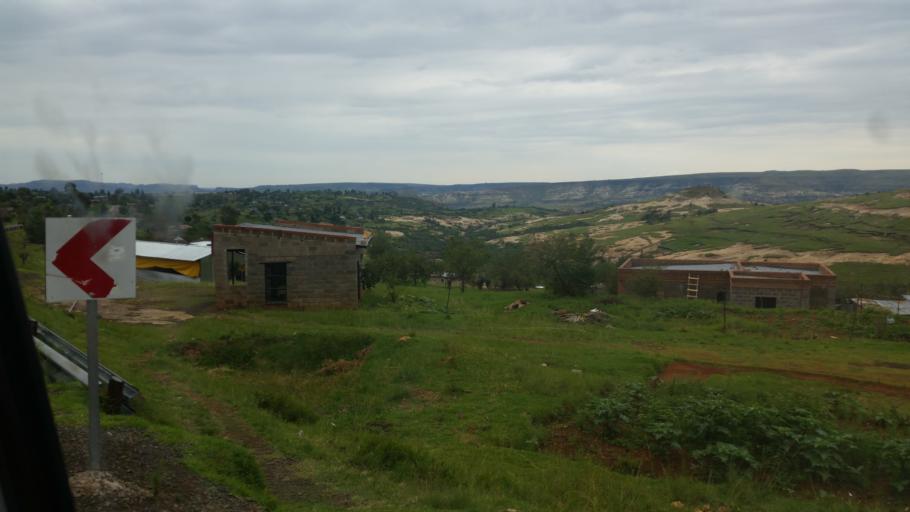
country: LS
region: Berea
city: Teyateyaneng
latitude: -29.1350
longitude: 27.9886
